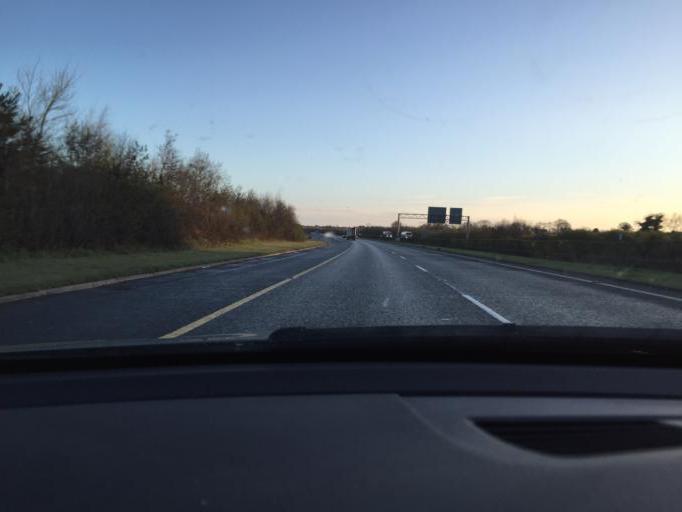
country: IE
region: Leinster
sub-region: Fingal County
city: Swords
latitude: 53.4928
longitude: -6.2029
